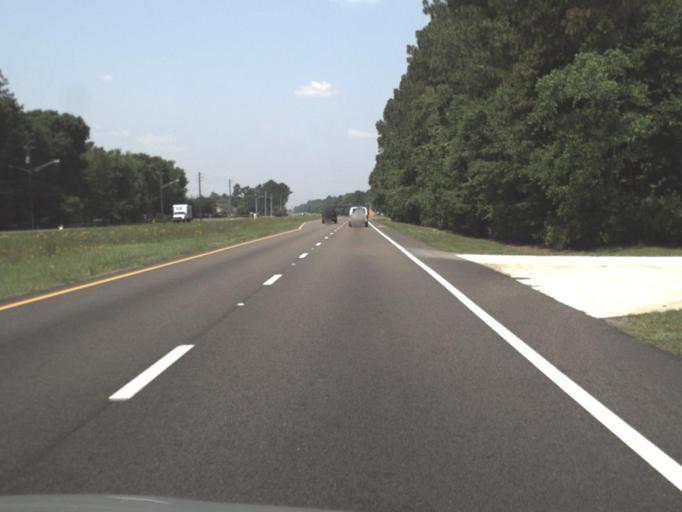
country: US
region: Florida
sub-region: Clay County
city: Bellair-Meadowbrook Terrace
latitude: 30.2779
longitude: -81.8250
